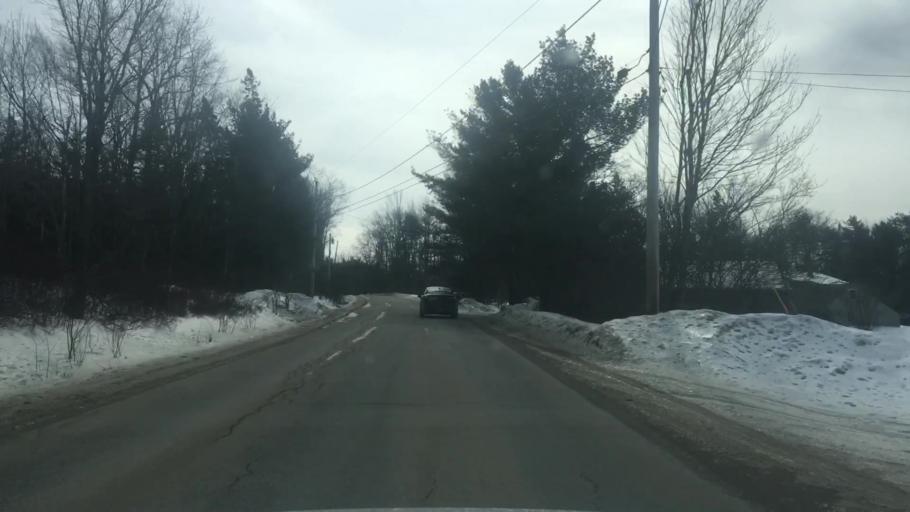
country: US
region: Maine
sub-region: Hancock County
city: Orland
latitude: 44.5865
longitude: -68.7259
